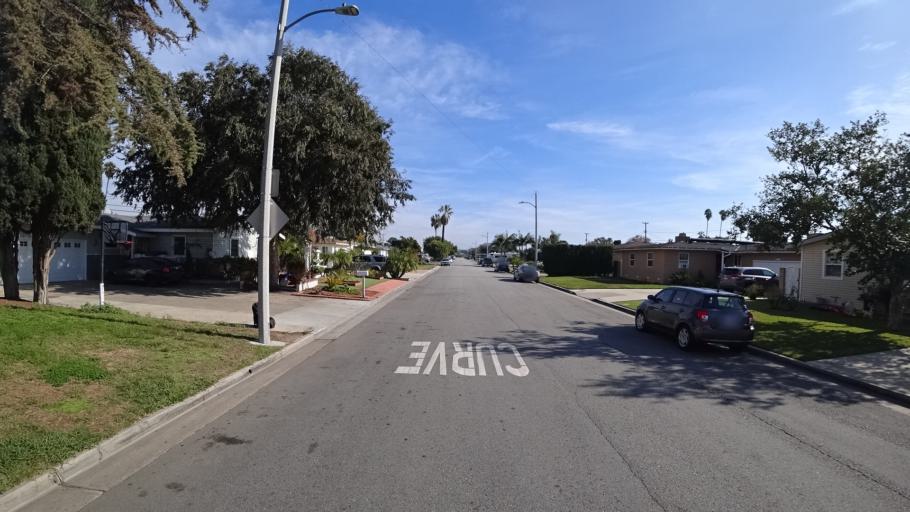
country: US
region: California
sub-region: Orange County
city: Garden Grove
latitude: 33.7908
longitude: -117.9313
